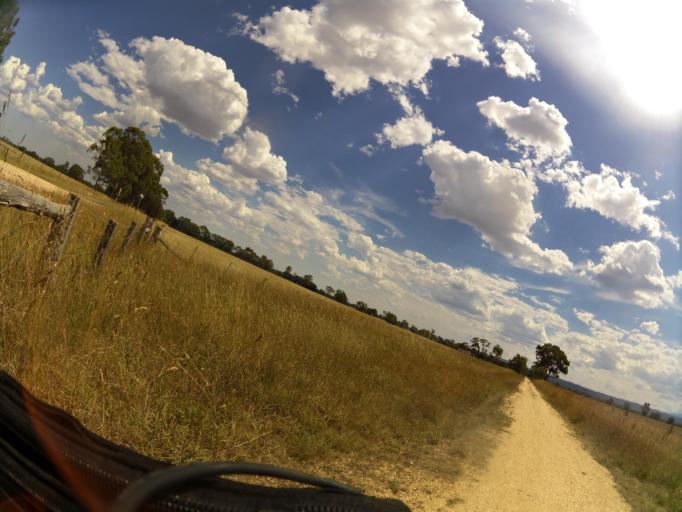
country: AU
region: Victoria
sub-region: Wellington
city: Heyfield
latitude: -37.9772
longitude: 146.7569
